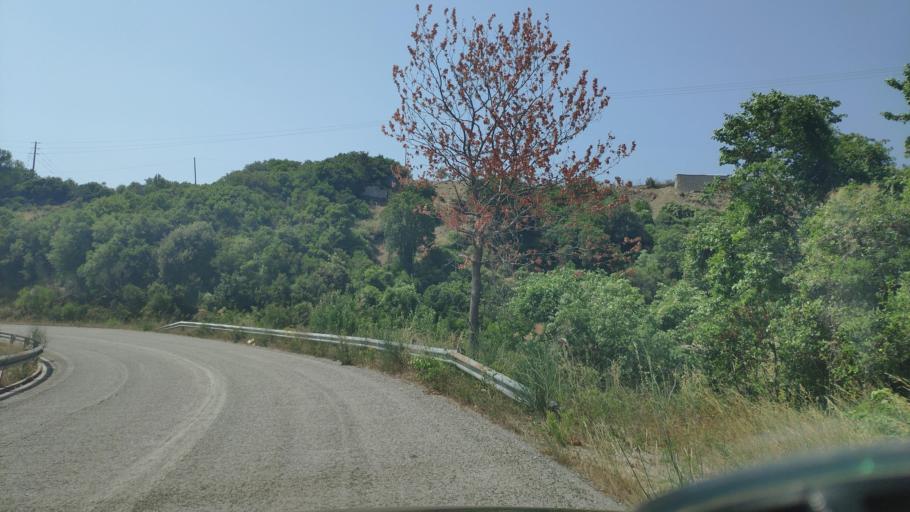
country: GR
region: Epirus
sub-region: Nomos Artas
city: Peta
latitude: 39.1791
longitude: 21.0854
